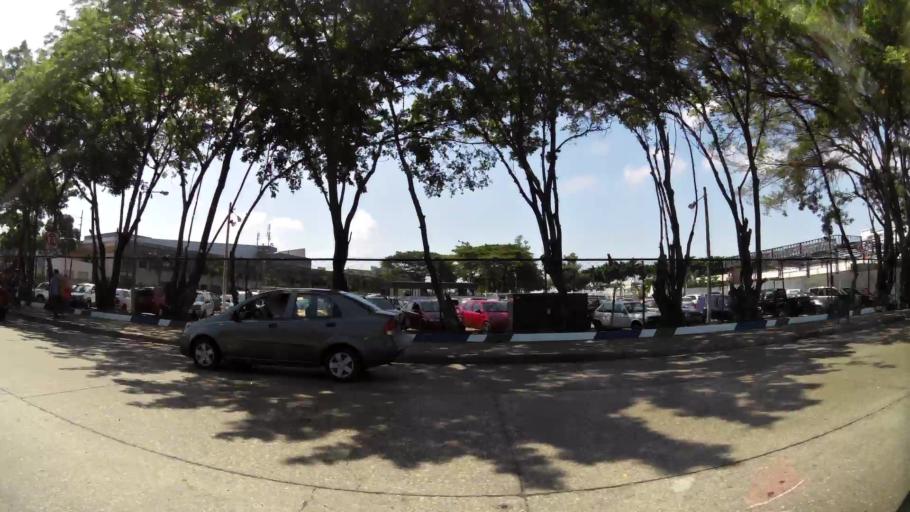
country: EC
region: Guayas
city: Guayaquil
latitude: -2.2310
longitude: -79.8997
